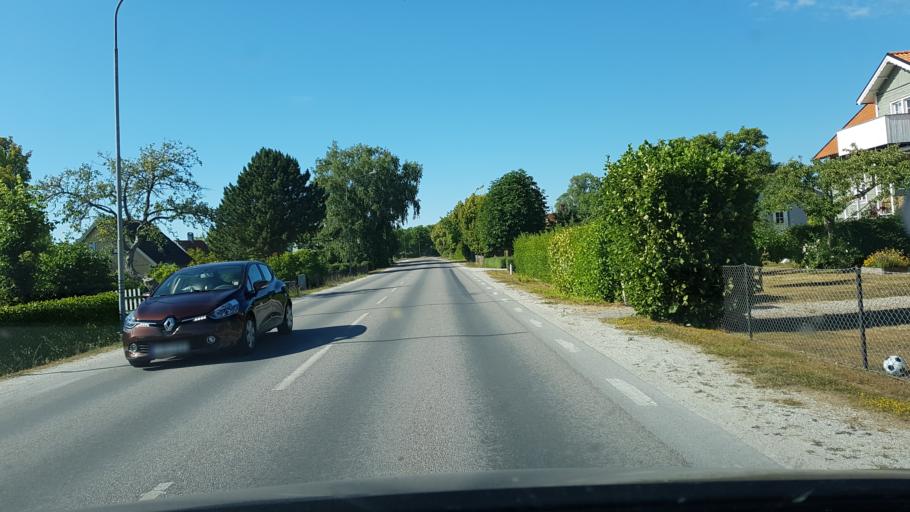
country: SE
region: Gotland
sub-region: Gotland
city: Klintehamn
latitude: 57.4353
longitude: 18.1459
